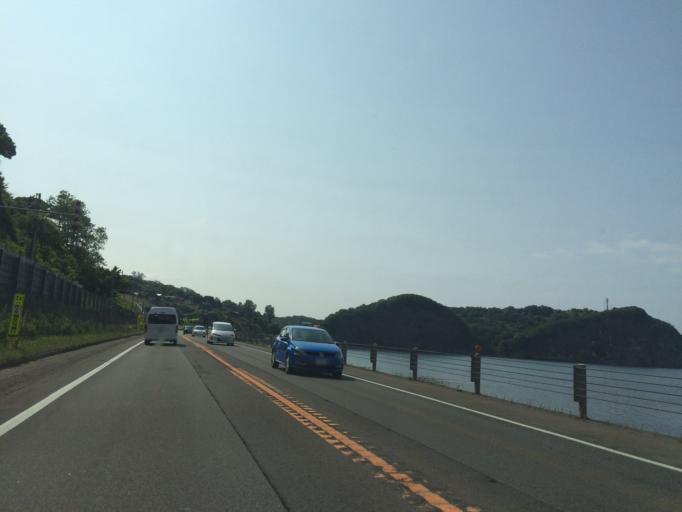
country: JP
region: Hokkaido
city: Yoichi
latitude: 43.2051
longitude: 140.8755
